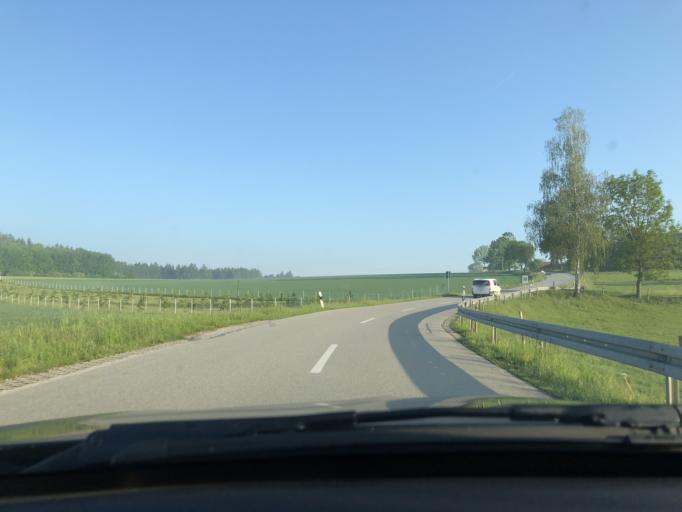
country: DE
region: Bavaria
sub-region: Upper Bavaria
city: Kirchdorf
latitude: 48.4750
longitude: 11.6359
